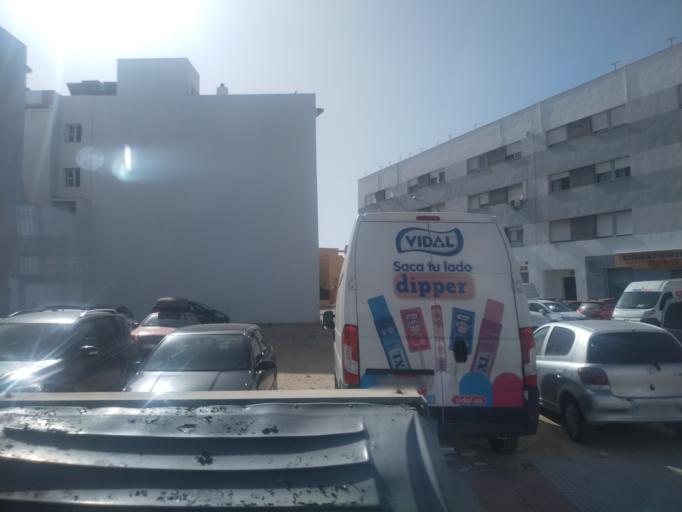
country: ES
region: Andalusia
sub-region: Provincia de Cadiz
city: San Fernando
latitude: 36.4511
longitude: -6.2161
